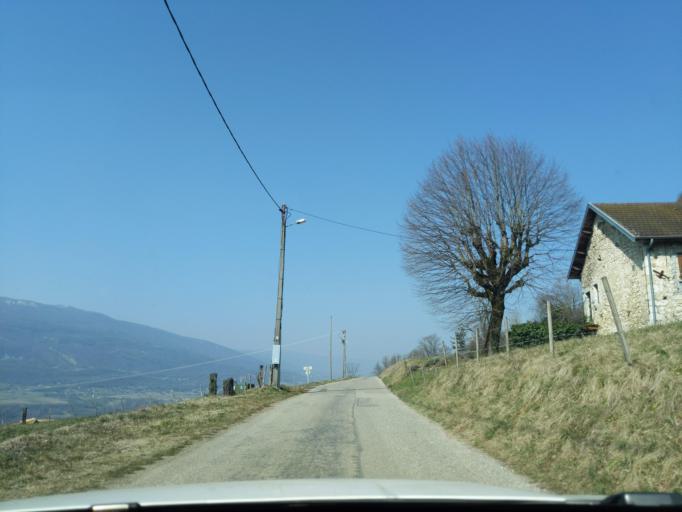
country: FR
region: Rhone-Alpes
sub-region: Departement de la Haute-Savoie
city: Moye
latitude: 45.9153
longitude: 5.8488
